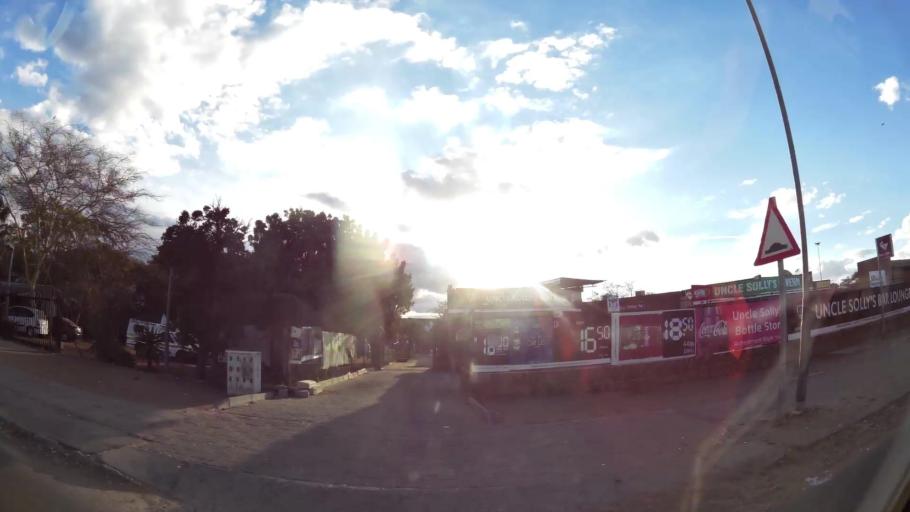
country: ZA
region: Limpopo
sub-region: Capricorn District Municipality
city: Polokwane
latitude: -23.9042
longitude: 29.4306
